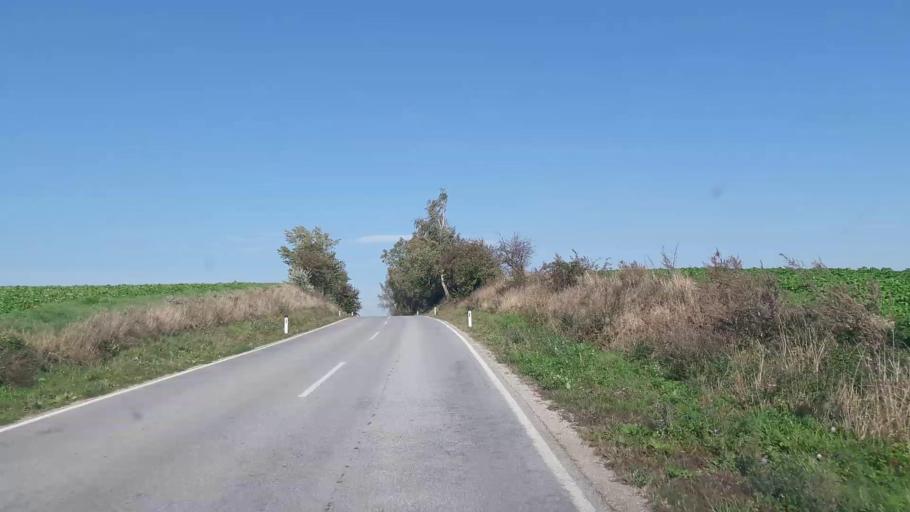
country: AT
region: Lower Austria
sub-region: Politischer Bezirk Korneuburg
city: Ernstbrunn
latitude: 48.5144
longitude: 16.3601
